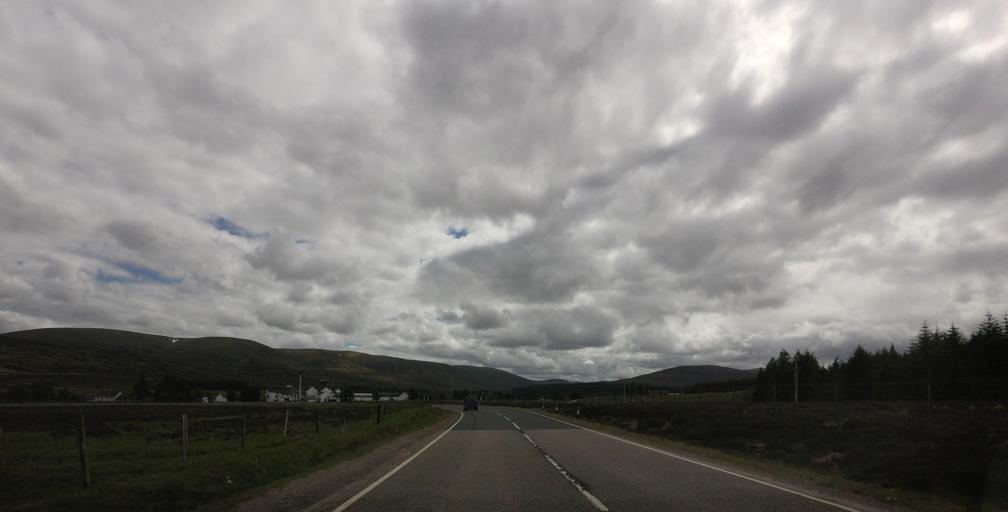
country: GB
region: Scotland
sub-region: Highland
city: Kingussie
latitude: 56.9431
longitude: -4.2426
